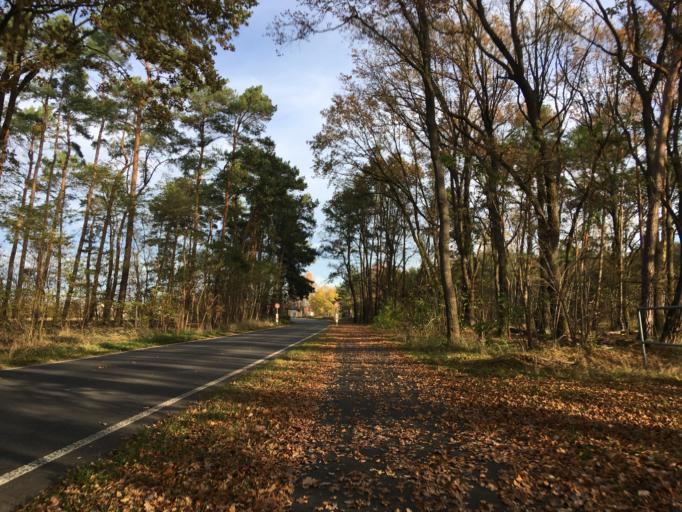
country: DE
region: Brandenburg
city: Luebben
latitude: 51.9626
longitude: 13.8850
